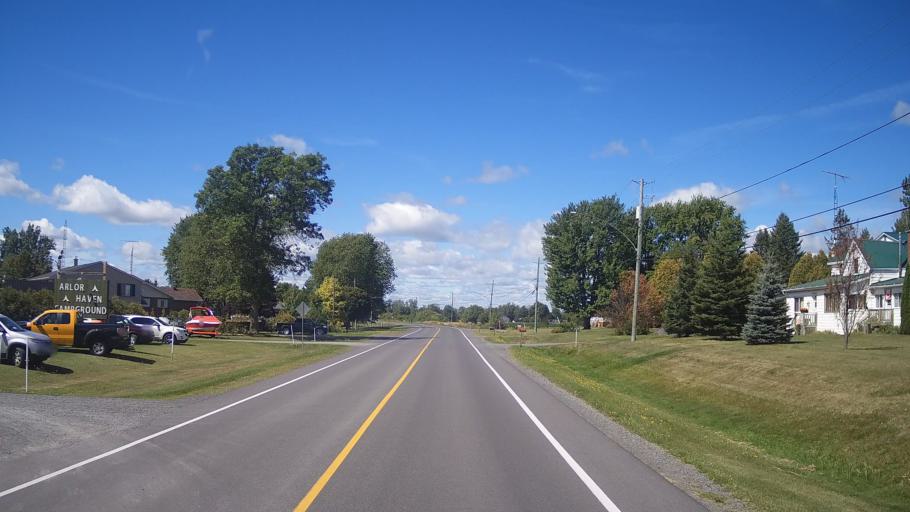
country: US
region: New York
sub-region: St. Lawrence County
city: Norfolk
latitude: 44.8839
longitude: -75.2087
